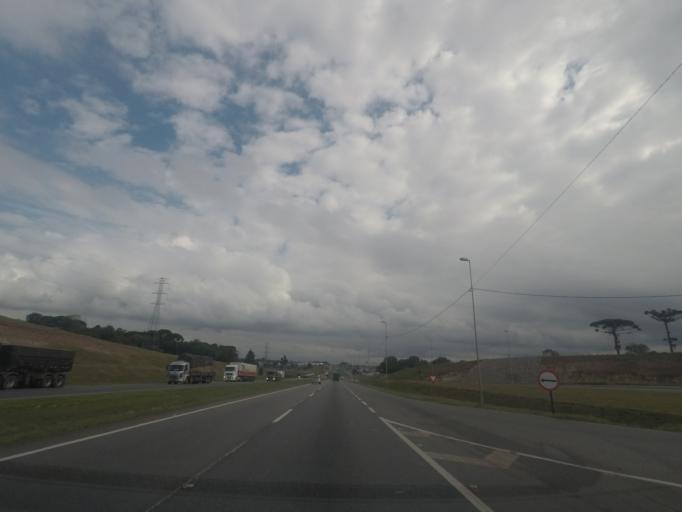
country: BR
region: Parana
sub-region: Piraquara
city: Piraquara
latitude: -25.4979
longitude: -49.1181
